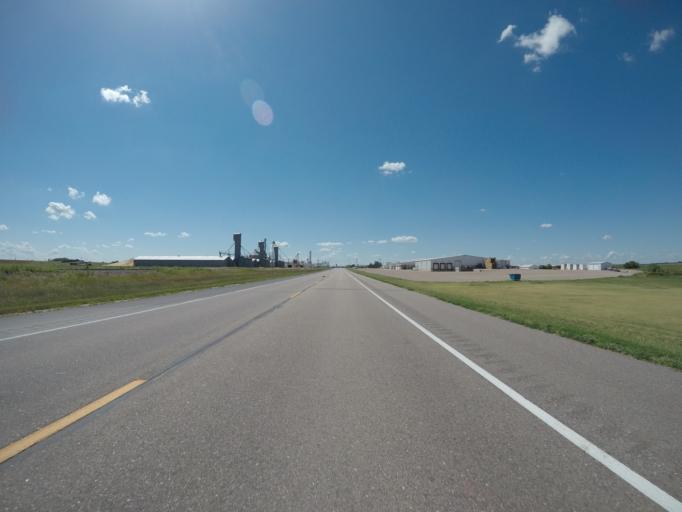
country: US
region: Nebraska
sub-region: Chase County
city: Imperial
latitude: 40.5037
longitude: -101.6198
